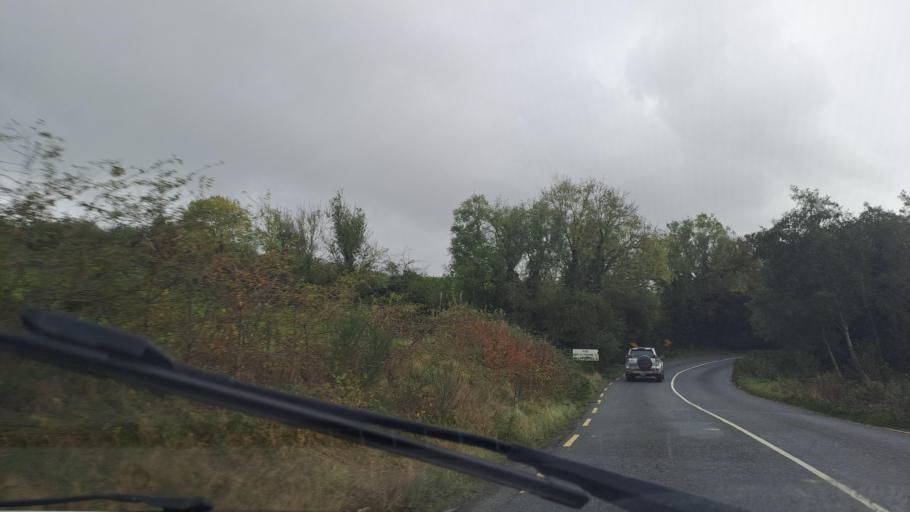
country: IE
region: Ulster
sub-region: An Cabhan
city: Bailieborough
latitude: 53.9237
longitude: -7.0005
